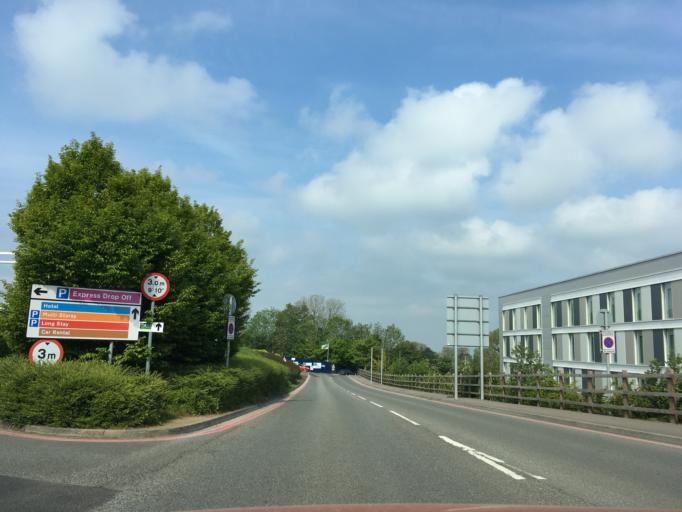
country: GB
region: England
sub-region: North Somerset
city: Butcombe
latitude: 51.3868
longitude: -2.7133
